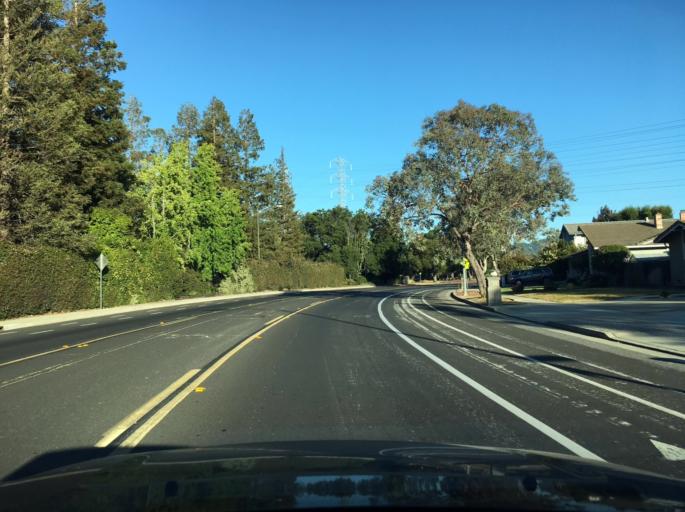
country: US
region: California
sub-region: Santa Clara County
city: Cambrian Park
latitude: 37.2337
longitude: -121.8851
